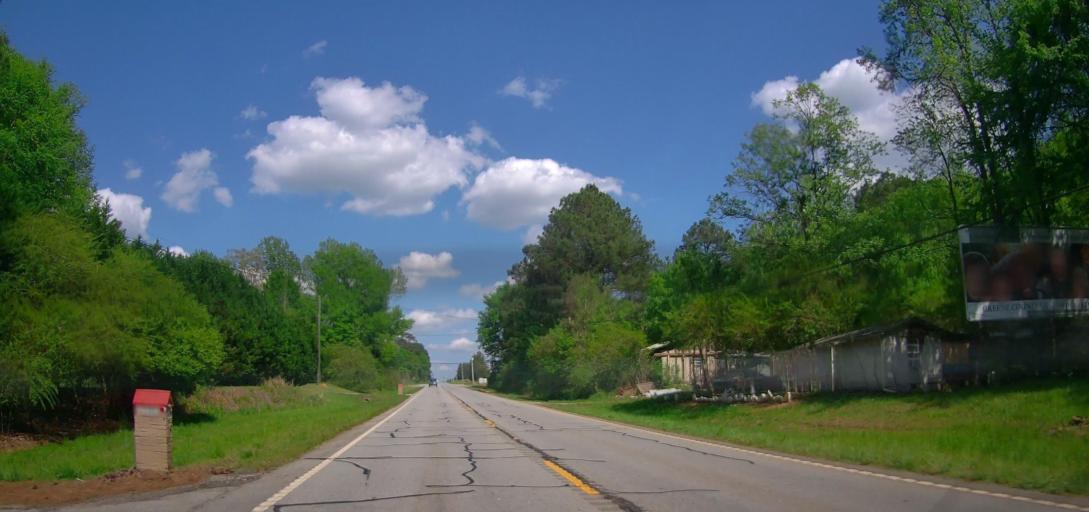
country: US
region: Georgia
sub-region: Greene County
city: Greensboro
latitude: 33.5765
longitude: -83.2074
